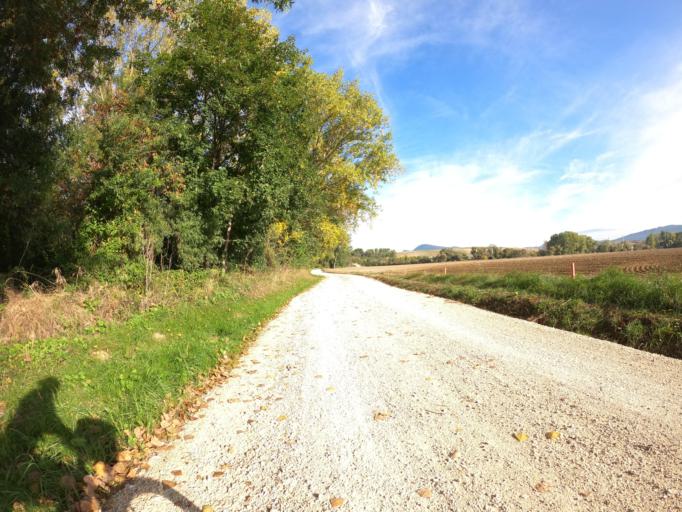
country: ES
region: Navarre
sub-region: Provincia de Navarra
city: Orkoien
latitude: 42.8139
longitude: -1.7390
